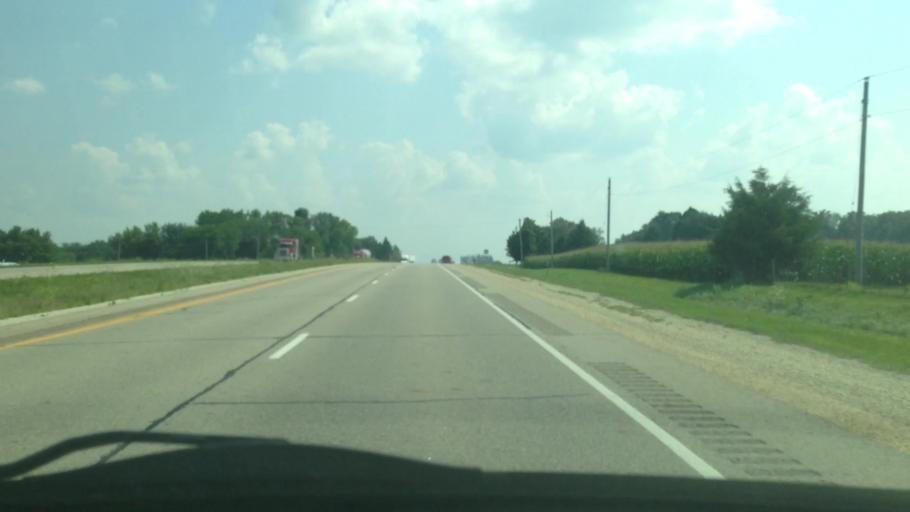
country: US
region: Iowa
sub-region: Bremer County
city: Denver
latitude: 42.6521
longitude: -92.3374
